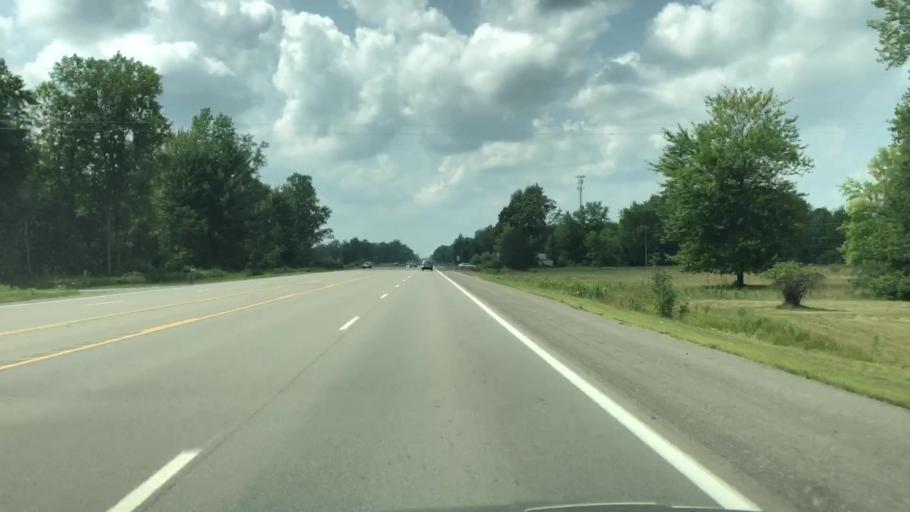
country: US
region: Michigan
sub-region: Midland County
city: Coleman
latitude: 43.6115
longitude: -84.5152
